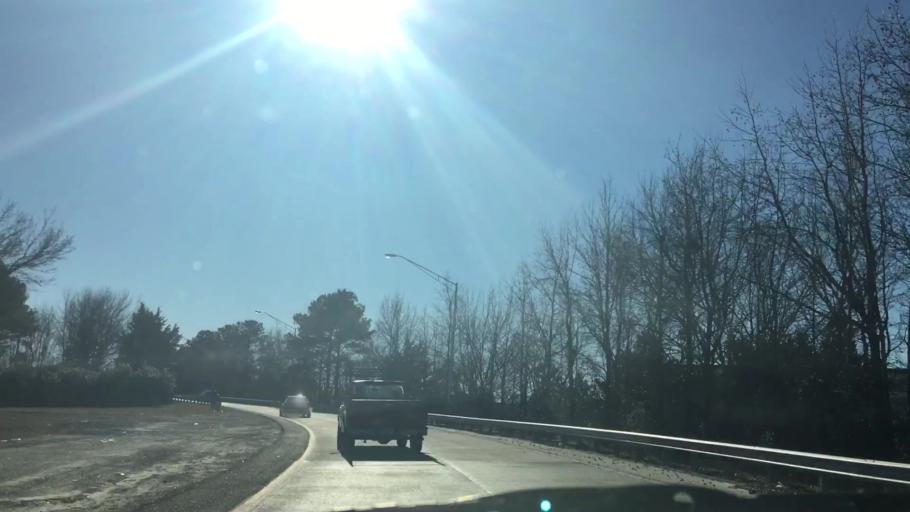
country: US
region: Virginia
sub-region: City of Newport News
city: Newport News
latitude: 37.0045
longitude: -76.4040
